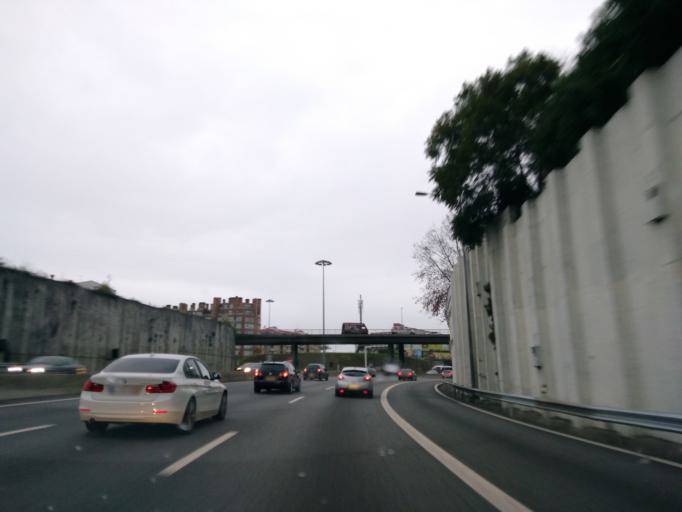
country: PT
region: Porto
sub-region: Maia
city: Pedroucos
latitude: 41.1668
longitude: -8.5856
